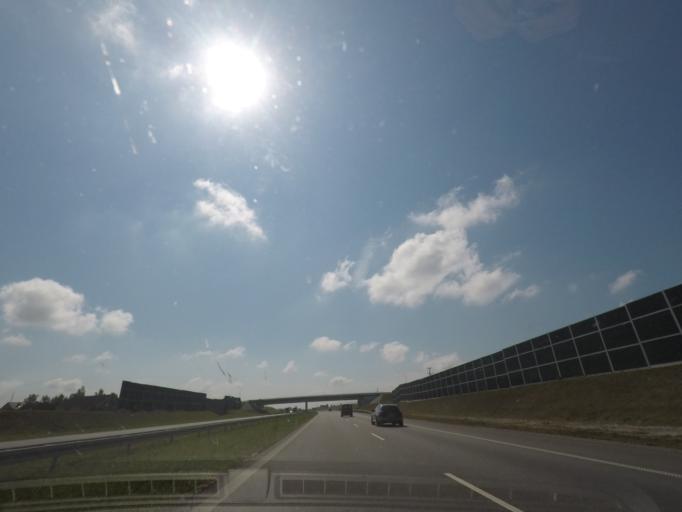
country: PL
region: Kujawsko-Pomorskie
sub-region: Powiat wloclawski
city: Czerniewice
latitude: 52.5034
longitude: 19.1181
